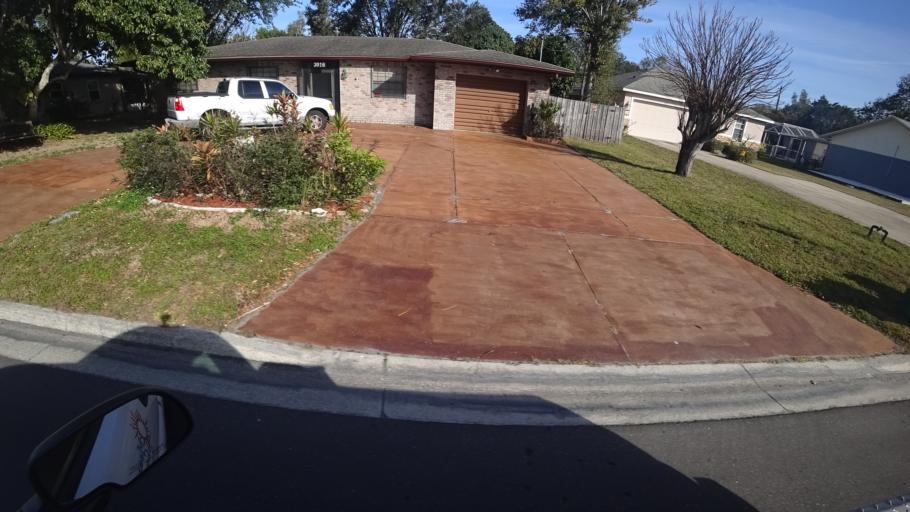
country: US
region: Florida
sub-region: Manatee County
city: Bradenton
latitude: 27.4847
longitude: -82.5925
